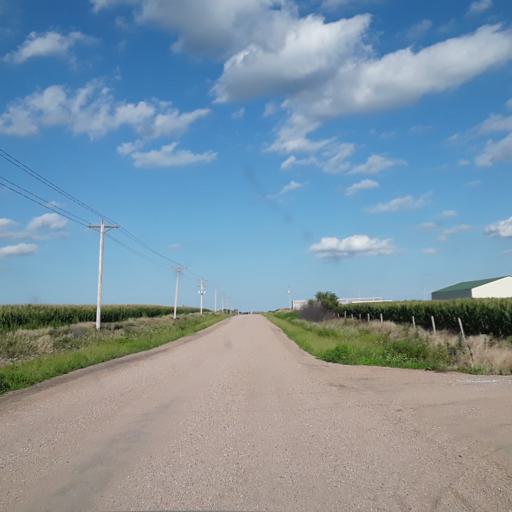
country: US
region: Nebraska
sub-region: Hall County
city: Wood River
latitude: 40.9168
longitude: -98.6015
